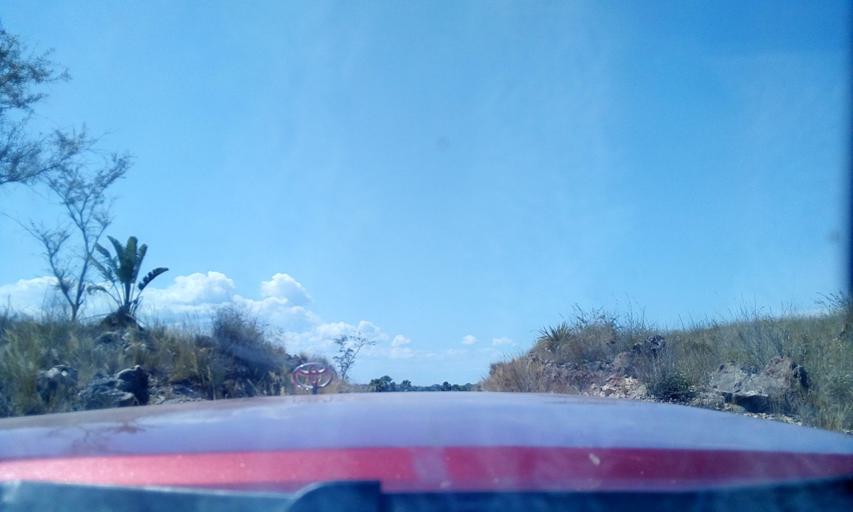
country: MG
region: Boeny
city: Sitampiky
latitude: -16.1299
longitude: 45.5006
